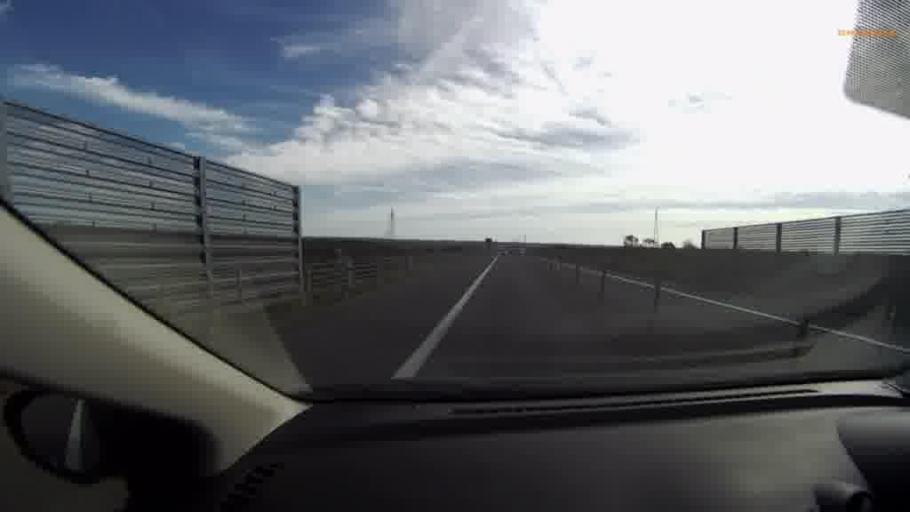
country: JP
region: Hokkaido
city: Kushiro
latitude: 43.0349
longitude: 144.3725
